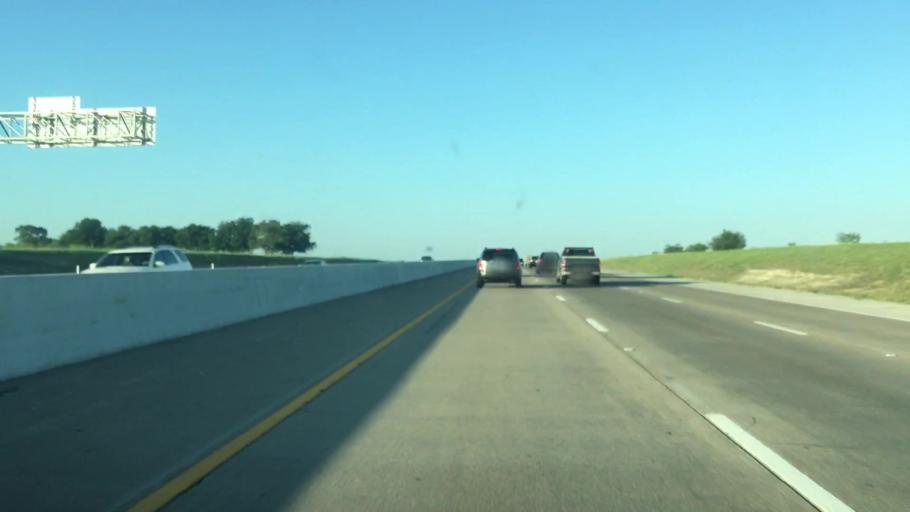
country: US
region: Texas
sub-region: Ellis County
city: Italy
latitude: 32.1678
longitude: -96.9164
